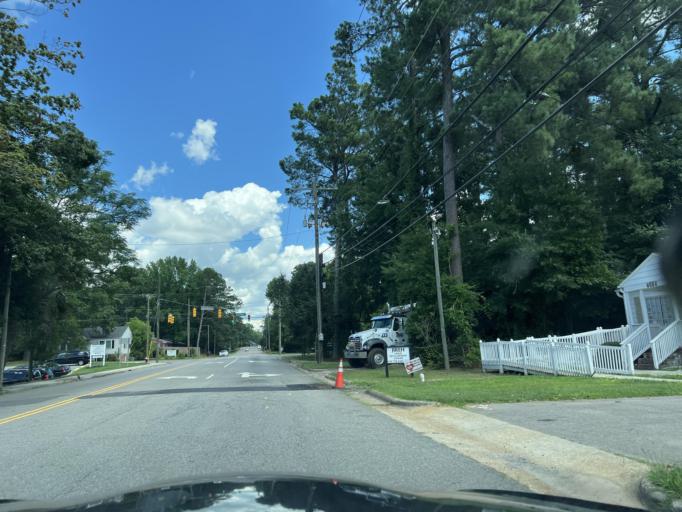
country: US
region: North Carolina
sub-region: Lee County
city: Sanford
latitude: 35.4661
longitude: -79.1649
